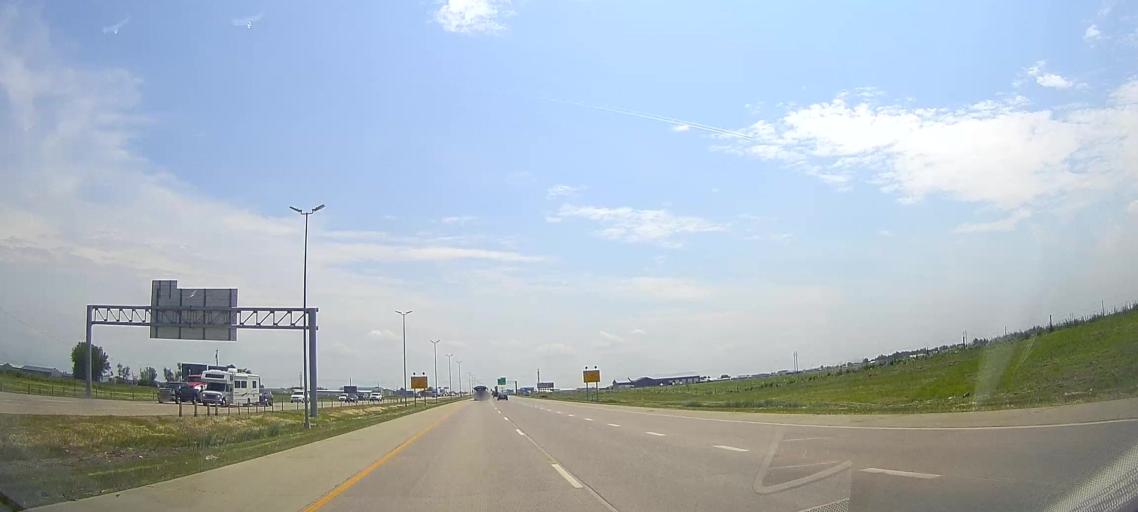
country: US
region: South Dakota
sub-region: Lincoln County
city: Tea
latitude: 43.4728
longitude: -96.7968
